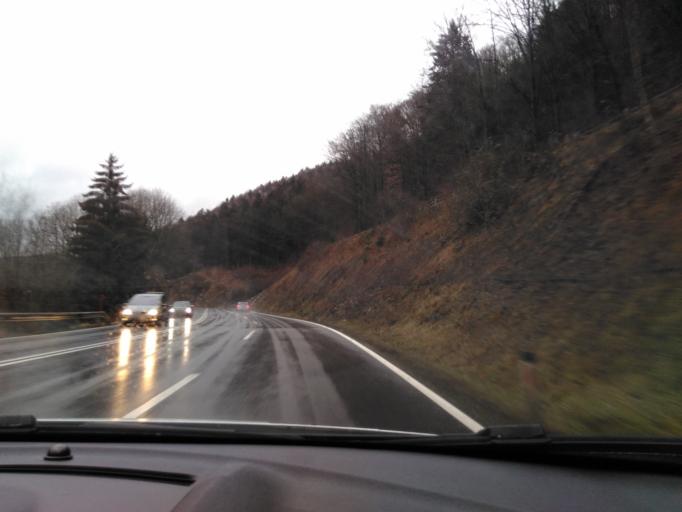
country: AT
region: Upper Austria
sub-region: Politischer Bezirk Urfahr-Umgebung
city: Kirchschlag bei Linz
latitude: 48.3831
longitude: 14.2938
